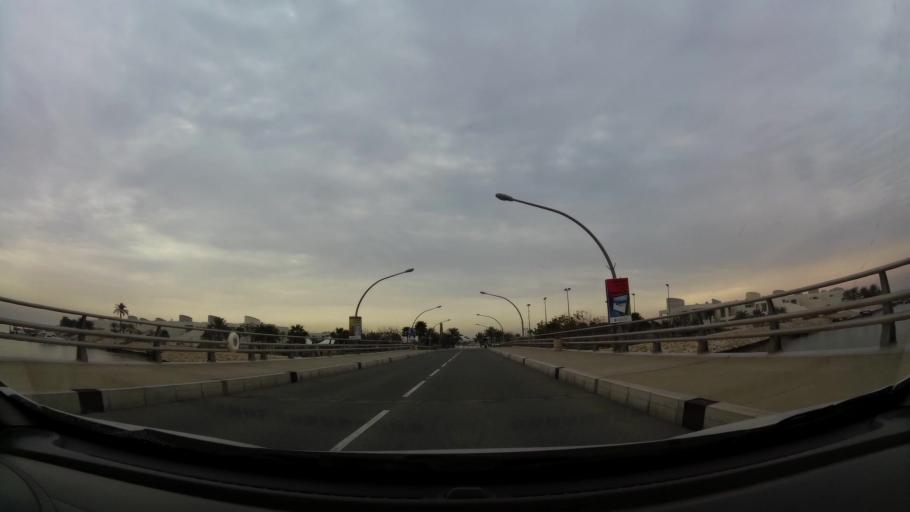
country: BH
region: Central Governorate
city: Dar Kulayb
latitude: 25.8313
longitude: 50.6171
